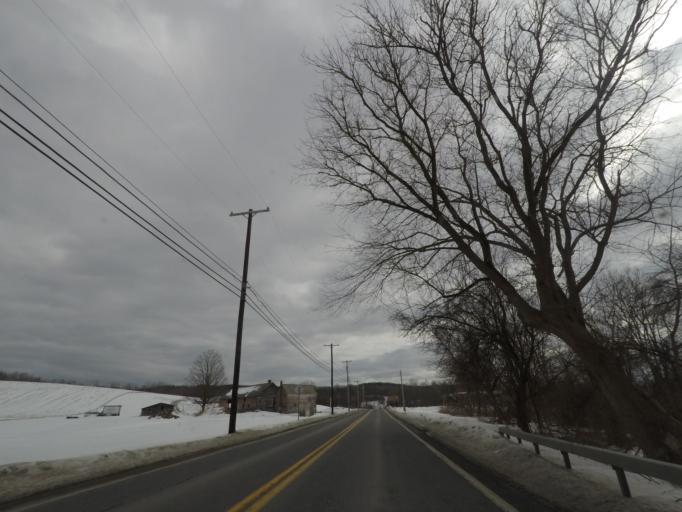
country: US
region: New York
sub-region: Washington County
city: Greenwich
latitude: 43.0835
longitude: -73.4864
